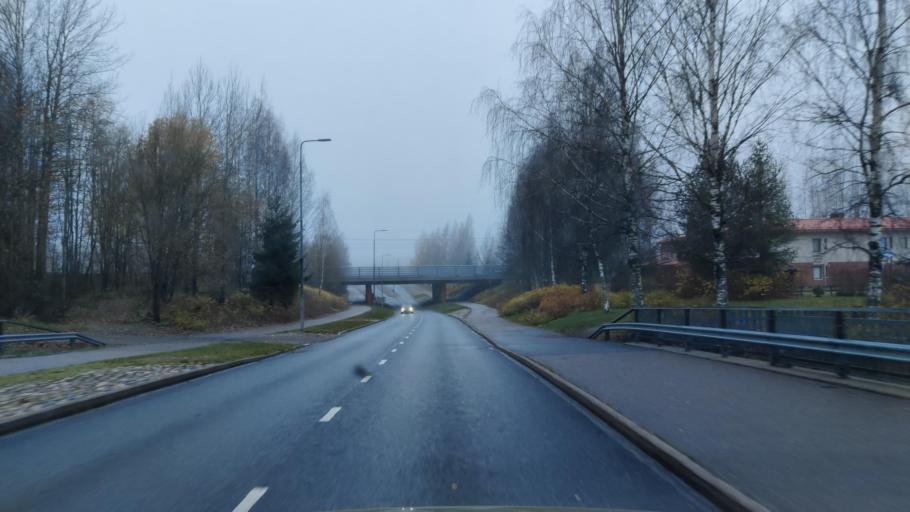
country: FI
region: Uusimaa
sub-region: Helsinki
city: Kerava
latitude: 60.3587
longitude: 25.0855
